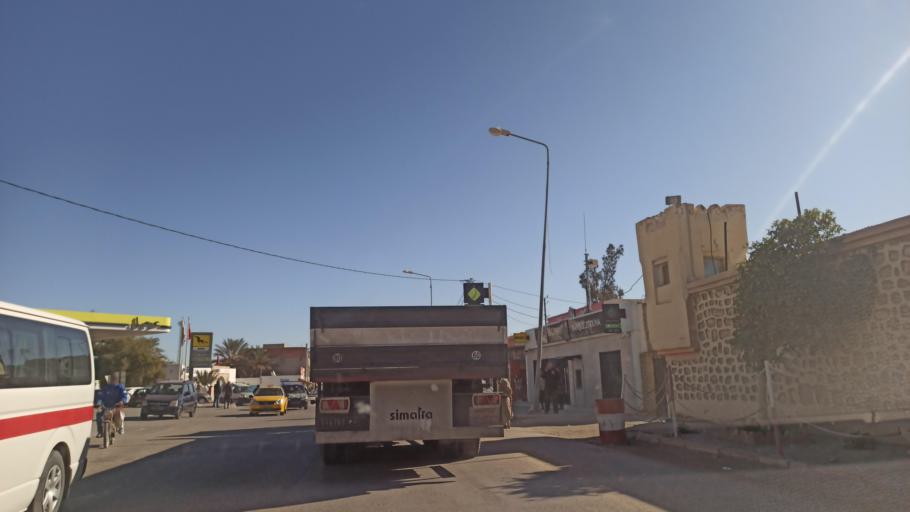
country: TN
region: Gafsa
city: Al Metlaoui
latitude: 34.3158
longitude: 8.4009
